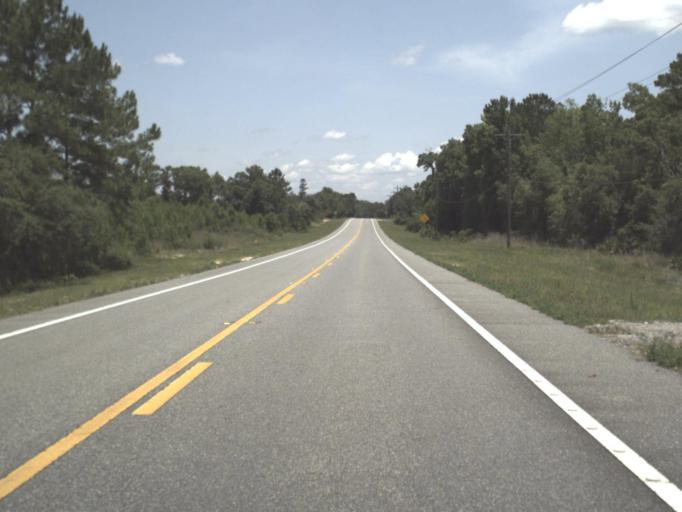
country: US
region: Florida
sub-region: Taylor County
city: Steinhatchee
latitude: 29.7032
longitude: -83.3578
